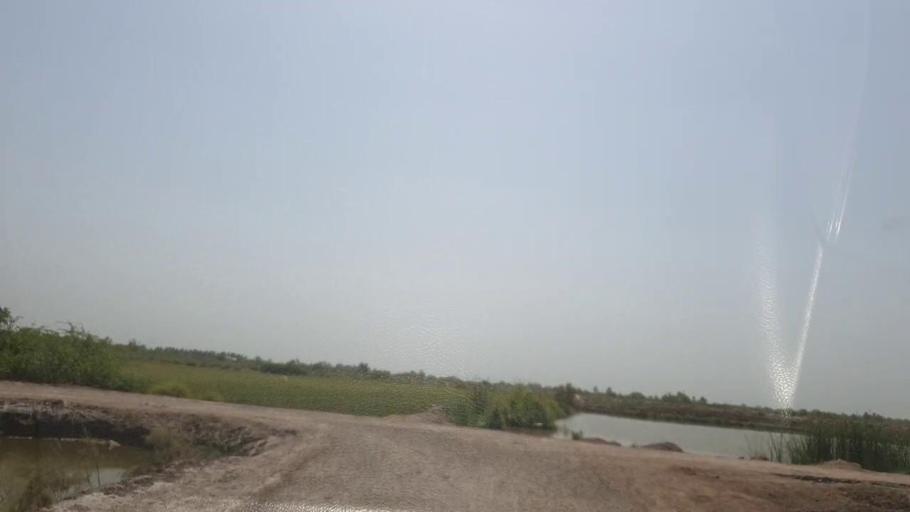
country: PK
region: Sindh
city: Gambat
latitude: 27.3151
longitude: 68.5409
